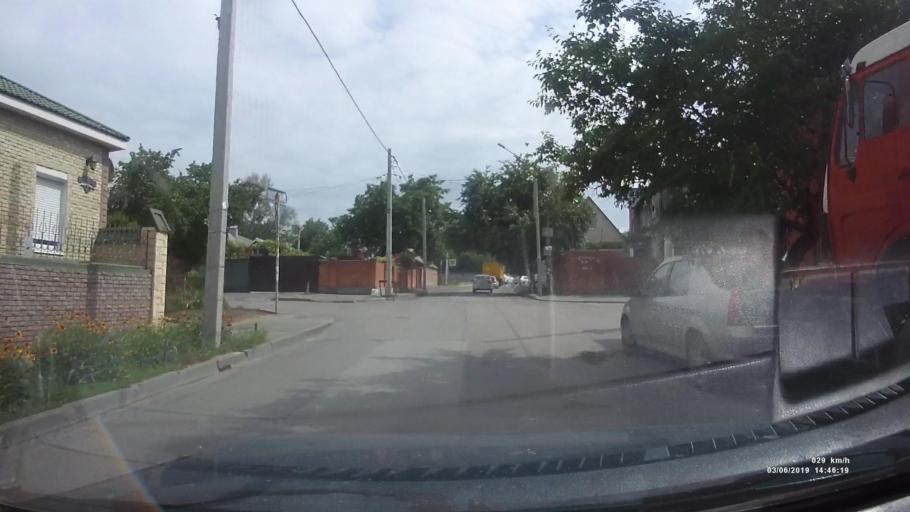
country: RU
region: Rostov
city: Rostov-na-Donu
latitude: 47.2451
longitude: 39.7241
